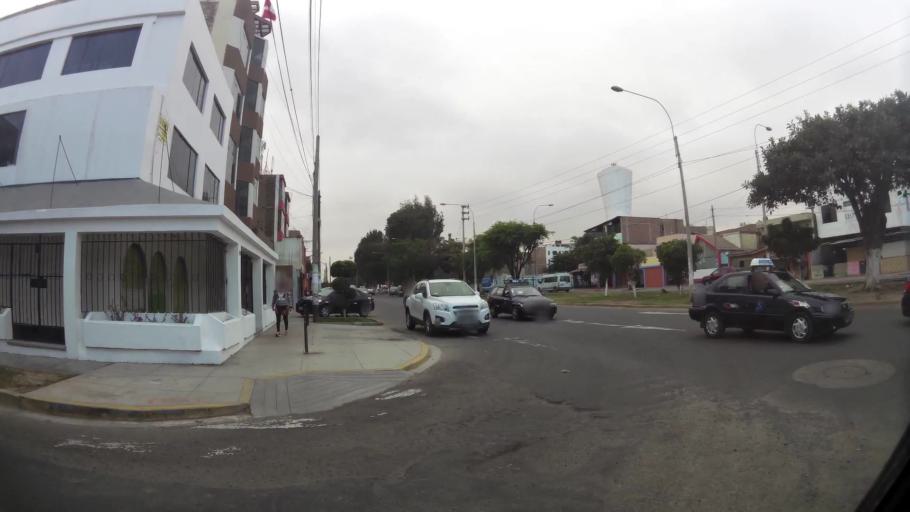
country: PE
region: La Libertad
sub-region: Provincia de Trujillo
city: Trujillo
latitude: -8.1003
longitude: -79.0270
